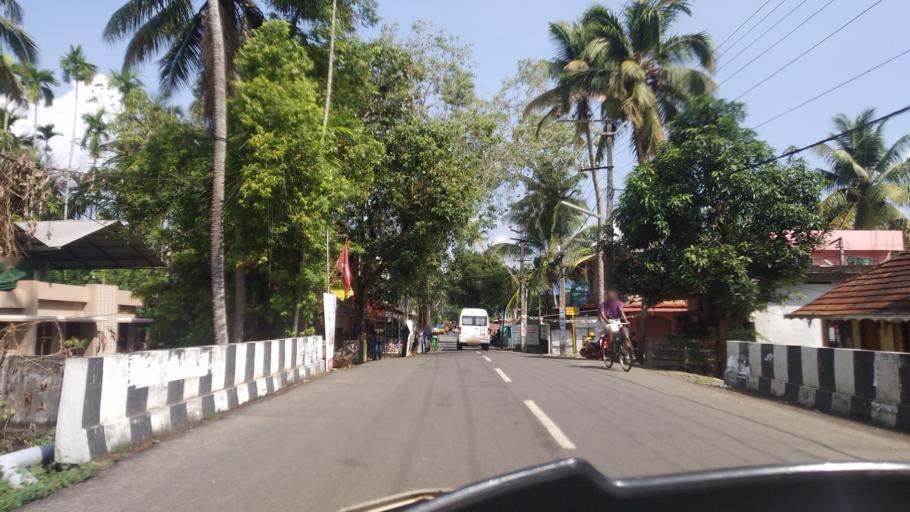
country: IN
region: Kerala
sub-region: Thrissur District
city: Kodungallur
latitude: 10.1349
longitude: 76.2208
